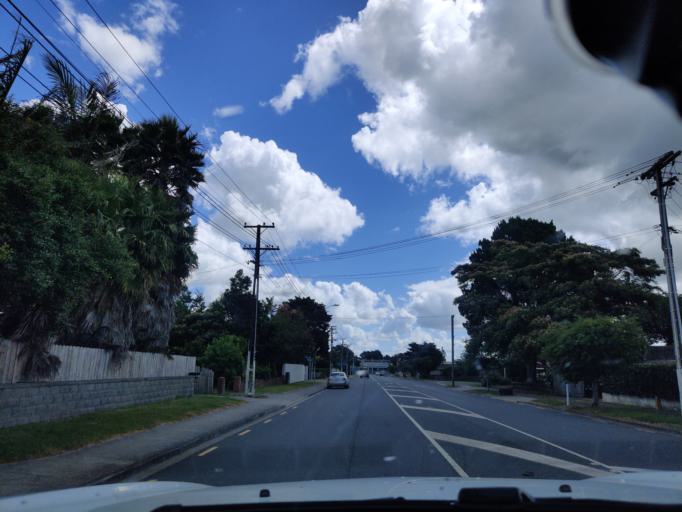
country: NZ
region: Auckland
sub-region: Auckland
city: Papakura
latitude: -37.0606
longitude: 174.9504
